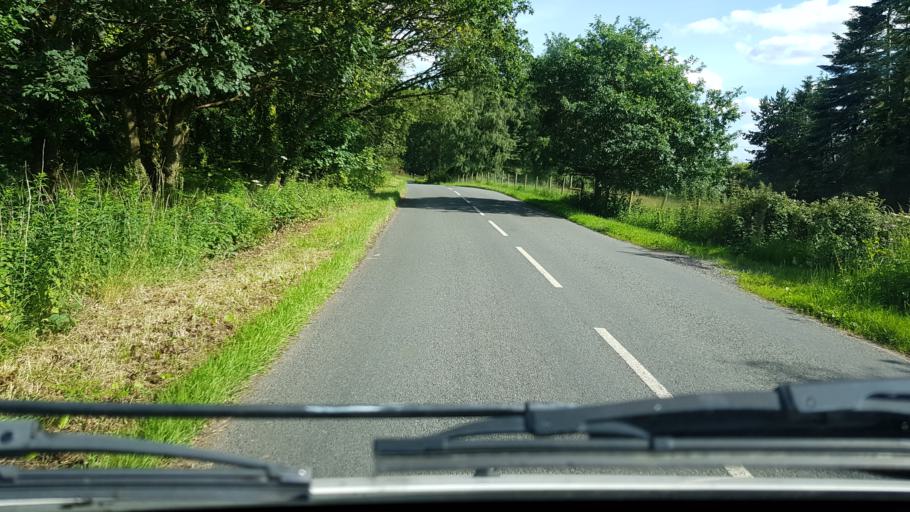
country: GB
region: England
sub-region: Worcestershire
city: Bewdley
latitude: 52.4051
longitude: -2.3086
